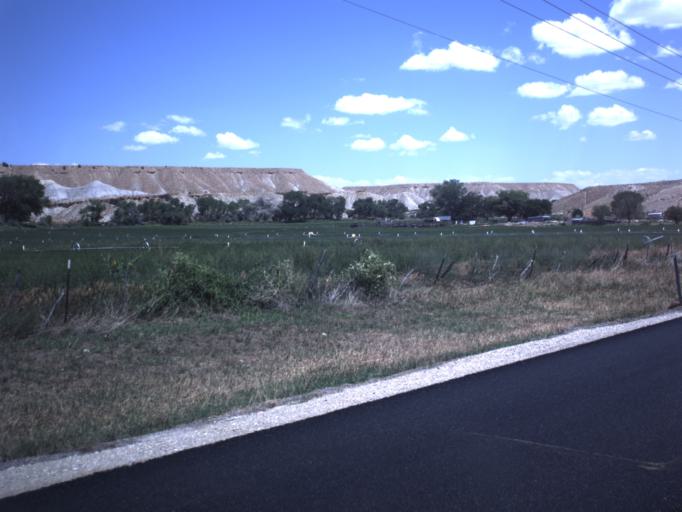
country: US
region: Utah
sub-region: Emery County
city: Orangeville
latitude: 39.2493
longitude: -111.0780
